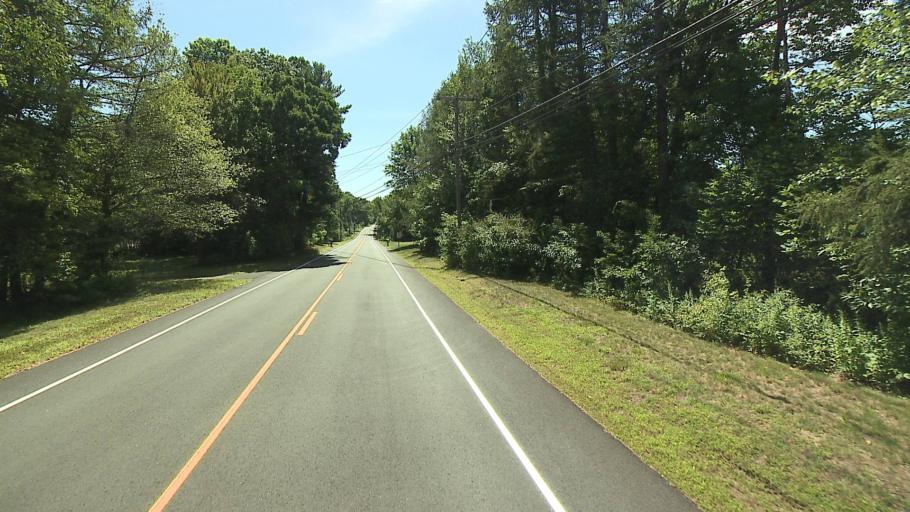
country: US
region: Connecticut
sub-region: Hartford County
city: North Granby
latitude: 41.9589
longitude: -72.9165
